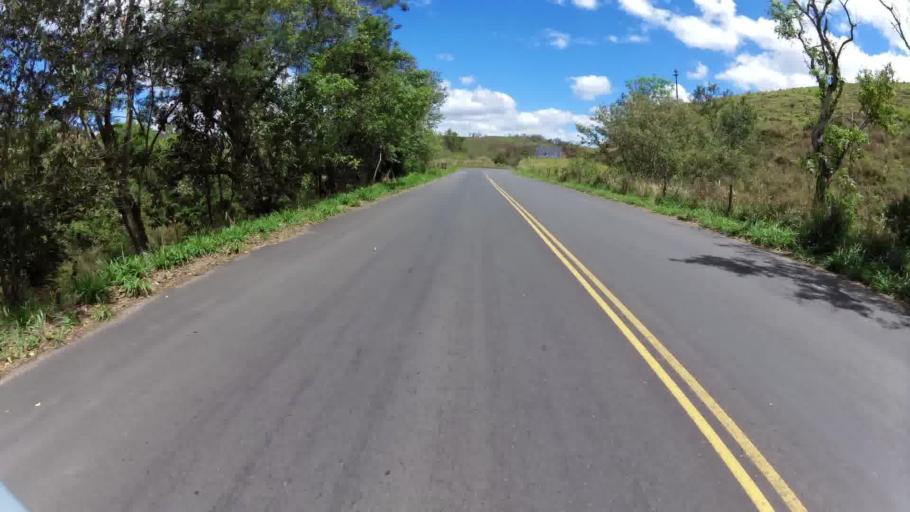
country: BR
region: Rio de Janeiro
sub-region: Itaperuna
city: Itaperuna
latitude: -21.3281
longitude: -41.8766
